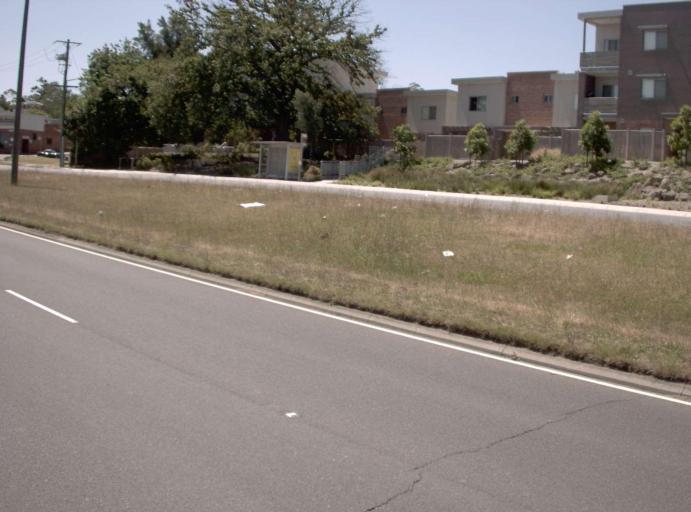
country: AU
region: Victoria
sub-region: Knox
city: Ferntree Gully
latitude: -37.8853
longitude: 145.2833
